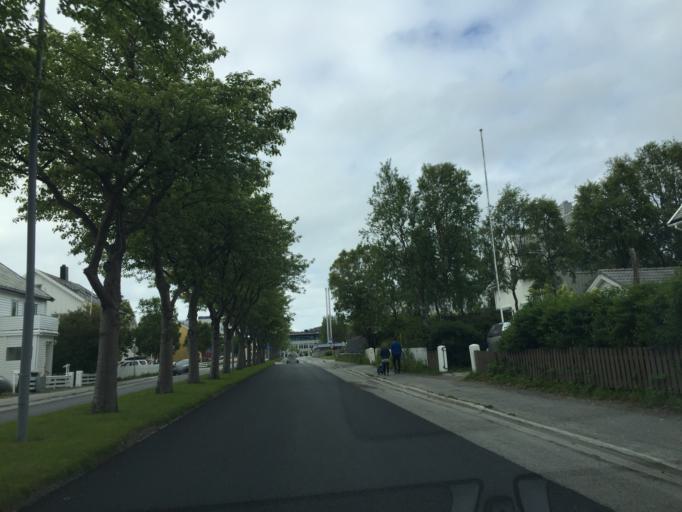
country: NO
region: Nordland
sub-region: Bodo
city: Bodo
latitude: 67.2789
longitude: 14.3778
